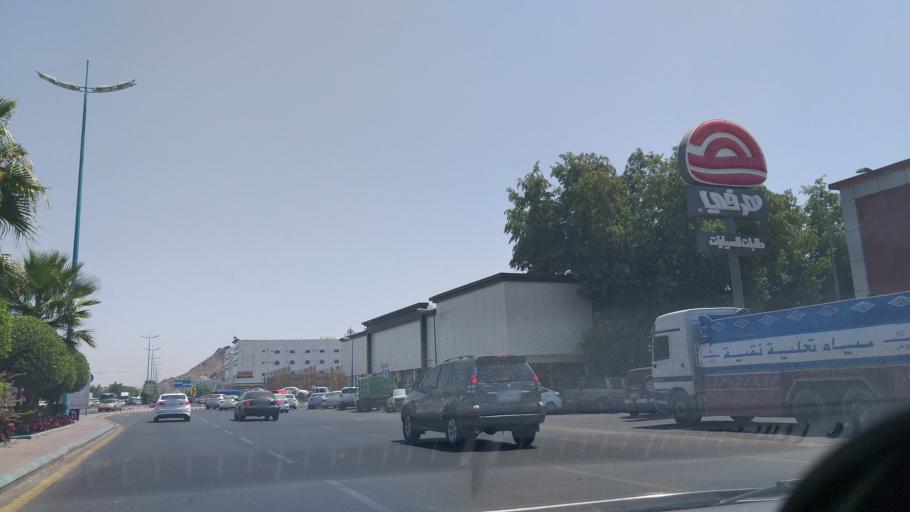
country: SA
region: Makkah
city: Ta'if
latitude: 21.2967
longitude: 40.4266
